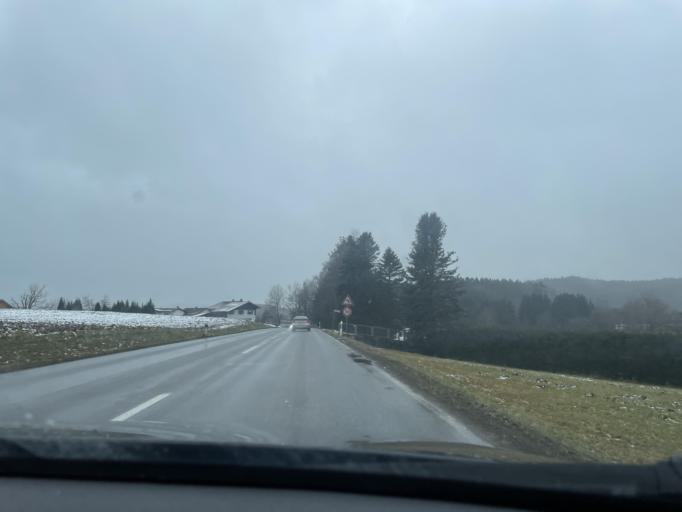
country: DE
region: Bavaria
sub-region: Upper Palatinate
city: Kotzting
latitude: 49.1977
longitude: 12.8560
